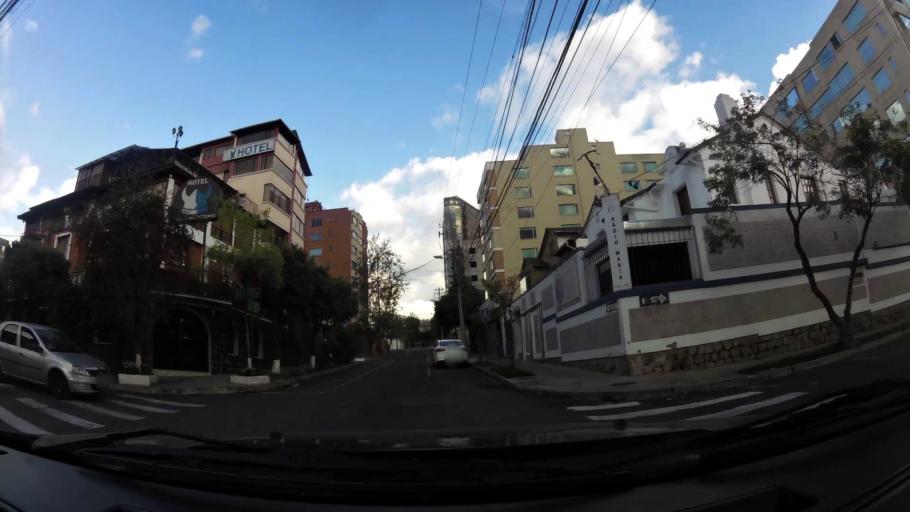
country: EC
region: Pichincha
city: Quito
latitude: -0.2041
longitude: -78.4875
